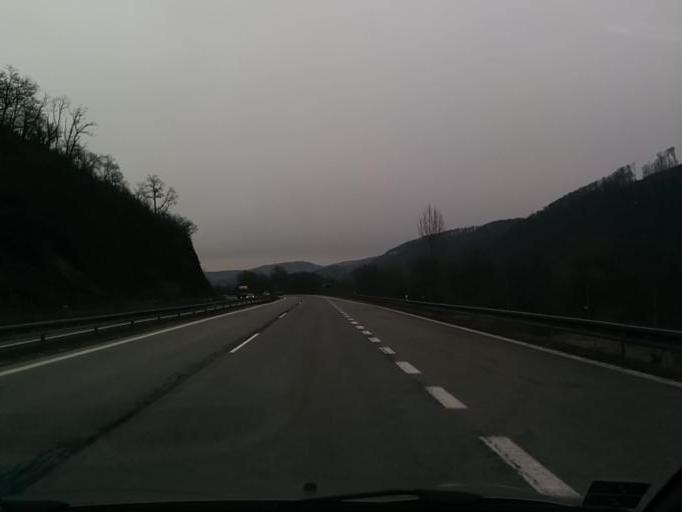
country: SK
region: Banskobystricky
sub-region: Okres Banska Bystrica
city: Zvolen
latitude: 48.5628
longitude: 19.0209
